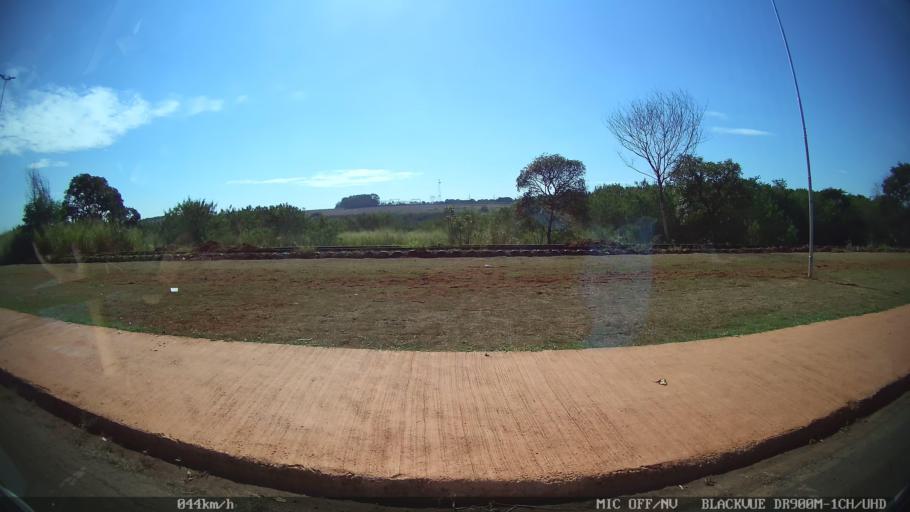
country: BR
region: Sao Paulo
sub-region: Santa Barbara D'Oeste
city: Santa Barbara d'Oeste
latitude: -22.7383
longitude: -47.4185
